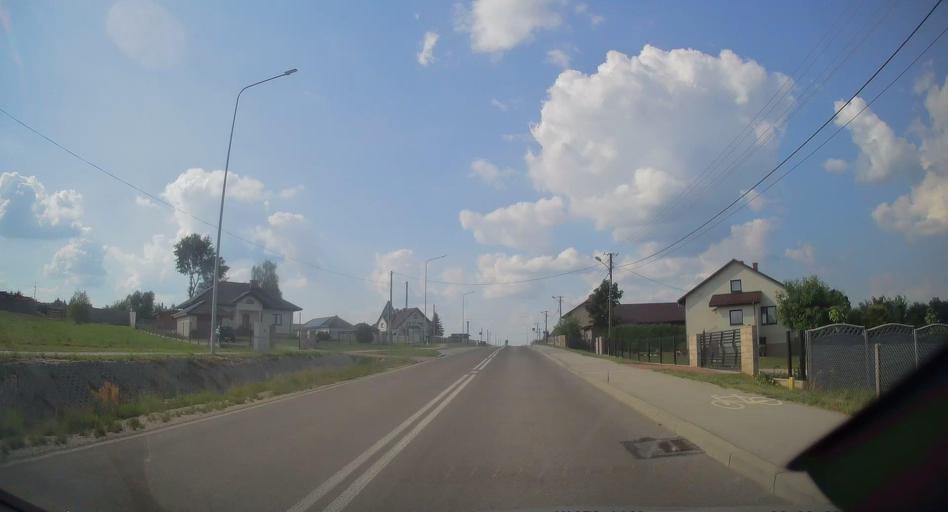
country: PL
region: Swietokrzyskie
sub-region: Powiat konecki
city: Radoszyce
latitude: 51.0325
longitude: 20.2880
